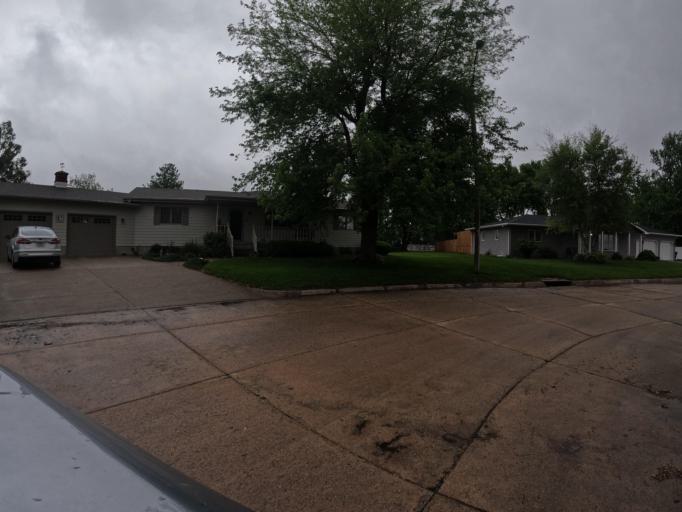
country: US
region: Nebraska
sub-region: Clay County
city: Harvard
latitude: 40.6238
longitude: -98.0906
